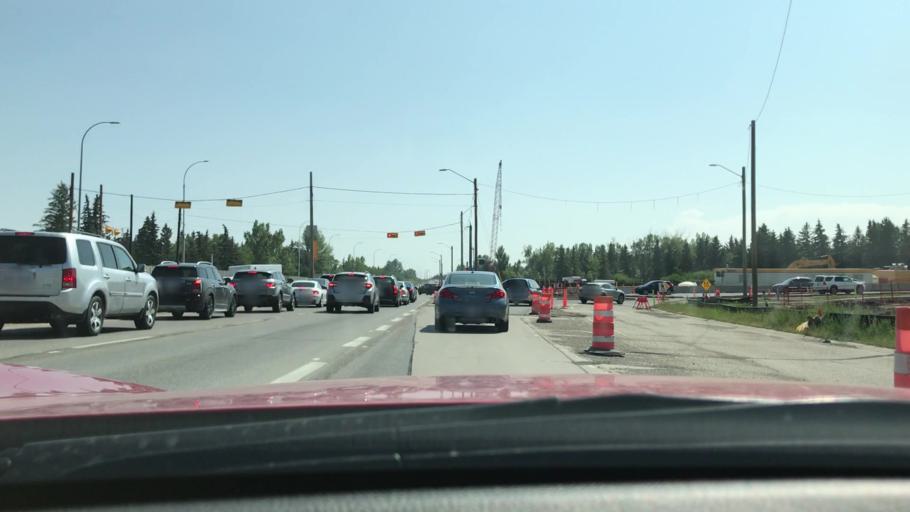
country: CA
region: Alberta
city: Calgary
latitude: 50.9733
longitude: -114.0953
